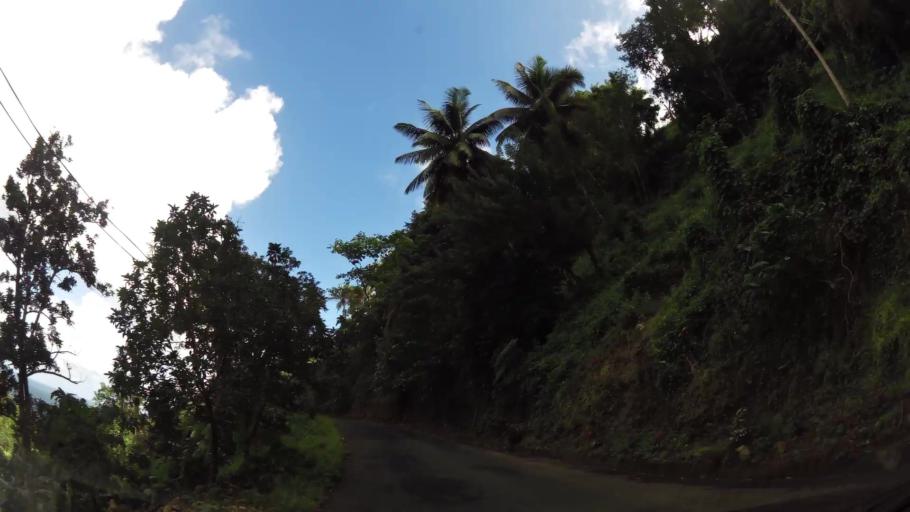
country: DM
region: Saint John
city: Portsmouth
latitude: 15.6179
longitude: -61.4160
